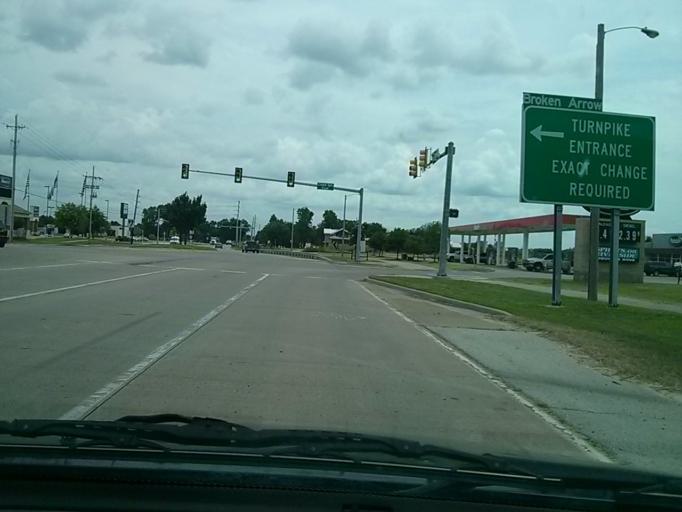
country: US
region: Oklahoma
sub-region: Tulsa County
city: Jenks
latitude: 36.0191
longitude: -95.9493
